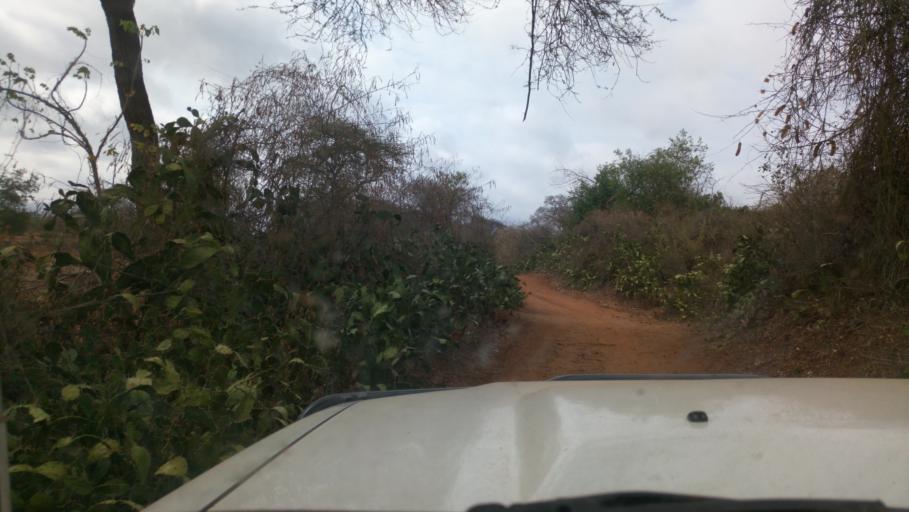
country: KE
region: Kitui
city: Kitui
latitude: -1.8560
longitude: 38.2554
